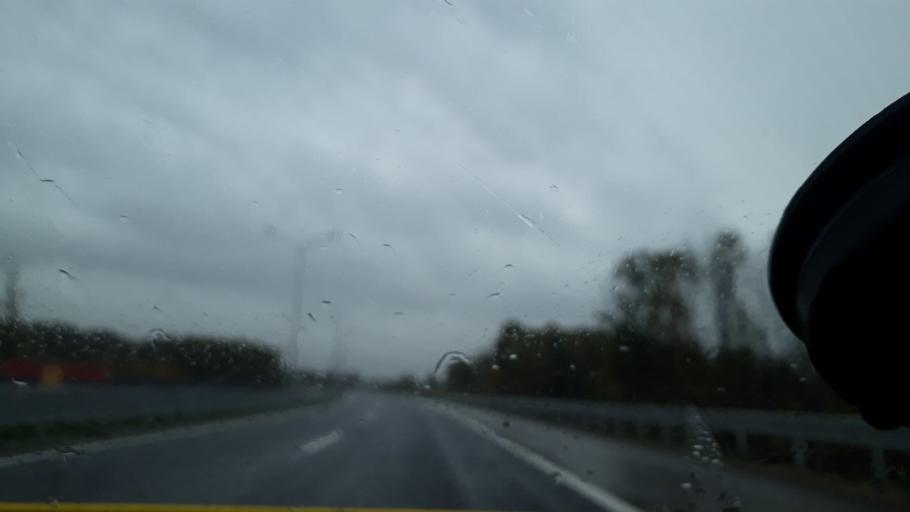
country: BA
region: Republika Srpska
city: Maglajani
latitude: 44.8968
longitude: 17.3615
